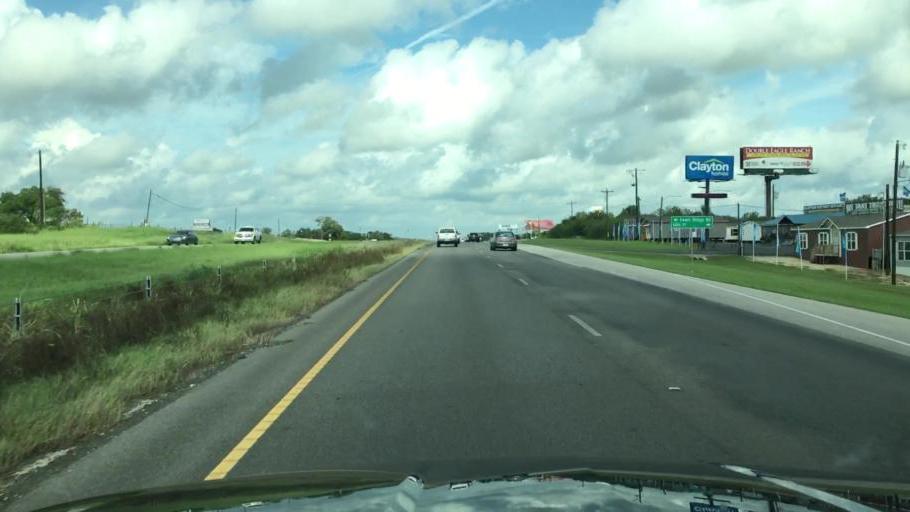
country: US
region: Texas
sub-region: Bastrop County
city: Wyldwood
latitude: 30.1581
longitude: -97.4987
